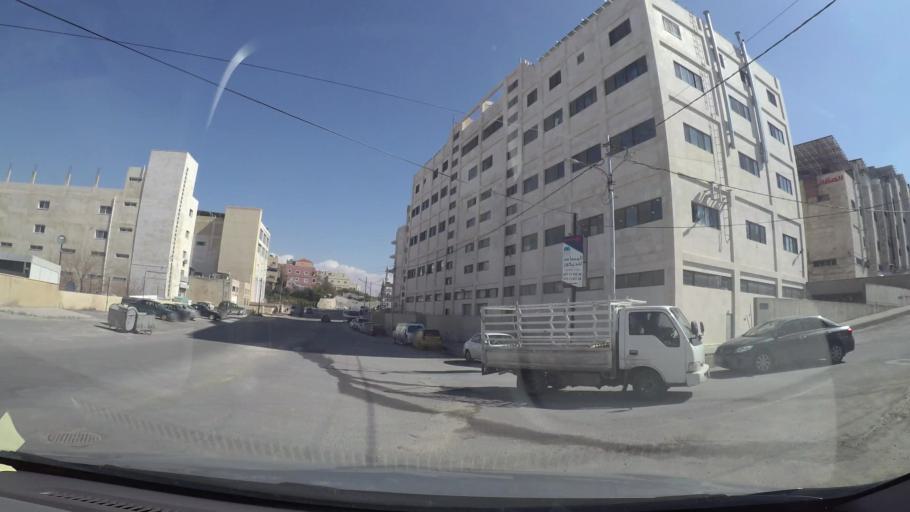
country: JO
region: Amman
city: Al Bunayyat ash Shamaliyah
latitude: 31.9110
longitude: 35.9121
